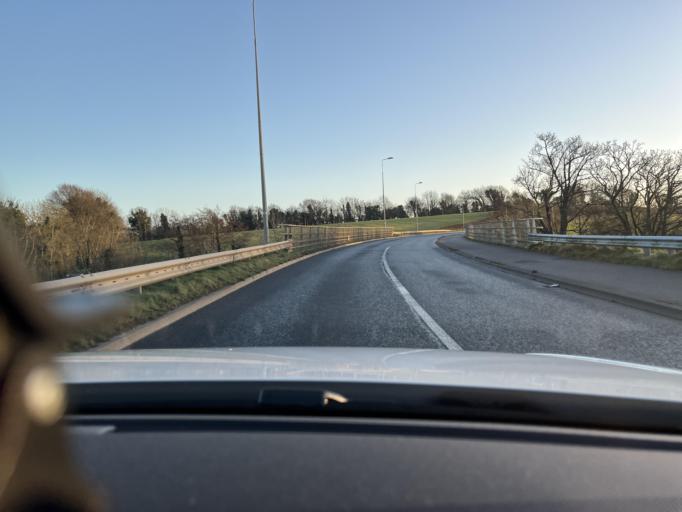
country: IE
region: Ulster
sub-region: An Cabhan
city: Ballyconnell
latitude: 54.1203
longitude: -7.5730
